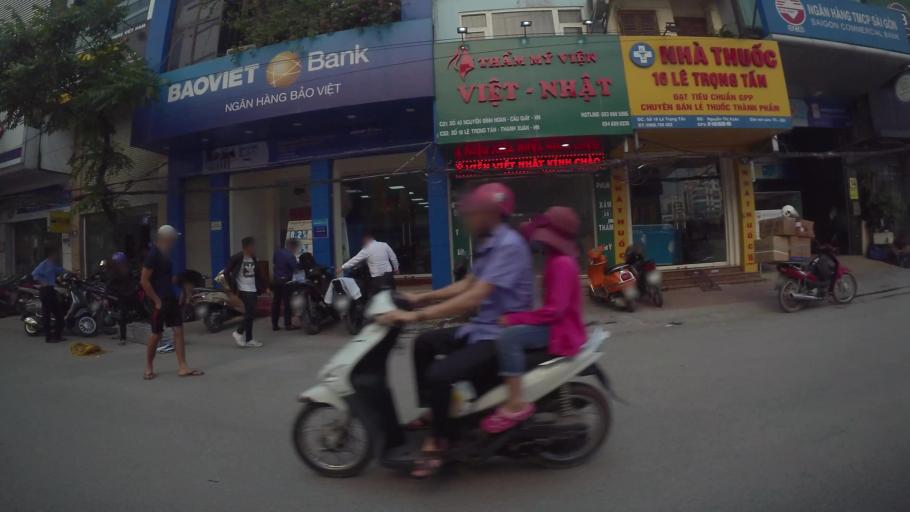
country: VN
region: Ha Noi
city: Dong Da
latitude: 21.0004
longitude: 105.8283
